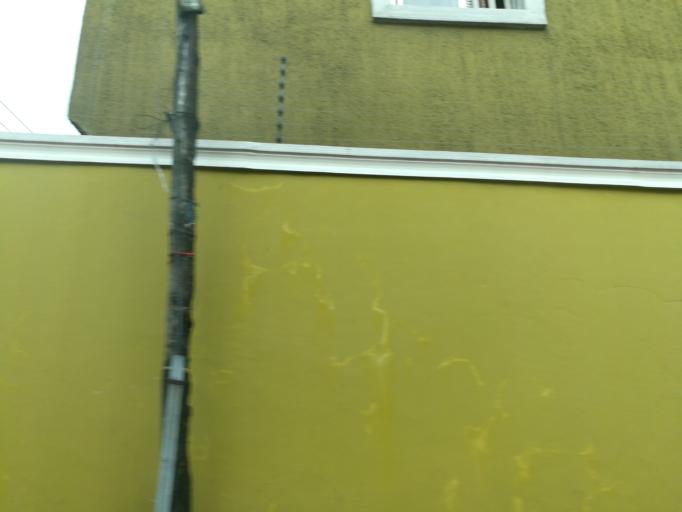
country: NG
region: Rivers
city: Port Harcourt
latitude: 4.8220
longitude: 7.0182
